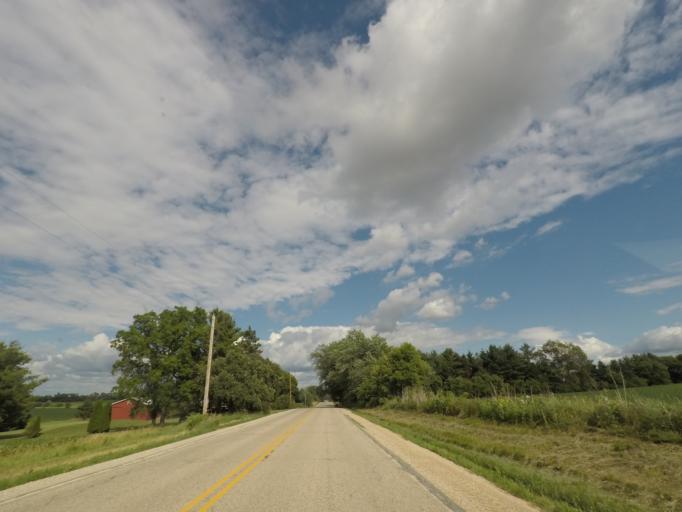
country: US
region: Wisconsin
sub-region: Rock County
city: Orfordville
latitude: 42.7082
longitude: -89.1780
